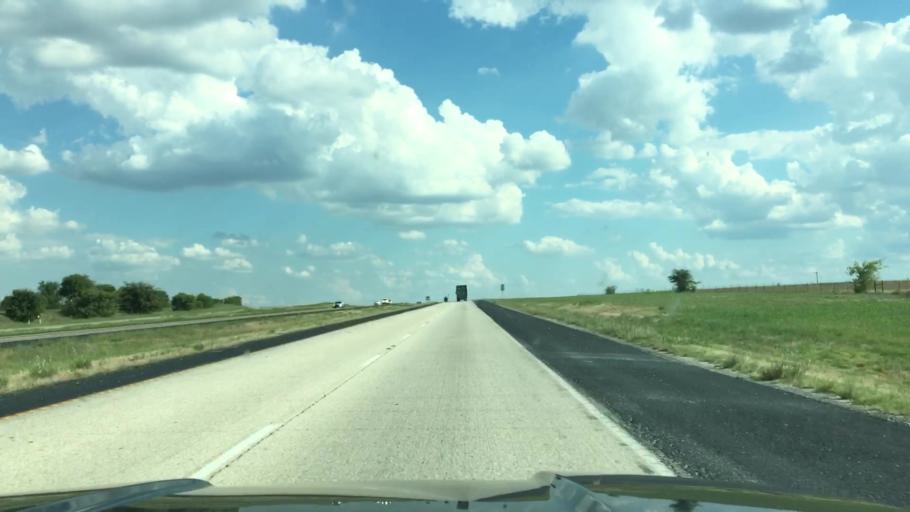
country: US
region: Texas
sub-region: Wise County
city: New Fairview
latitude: 33.1134
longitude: -97.4794
